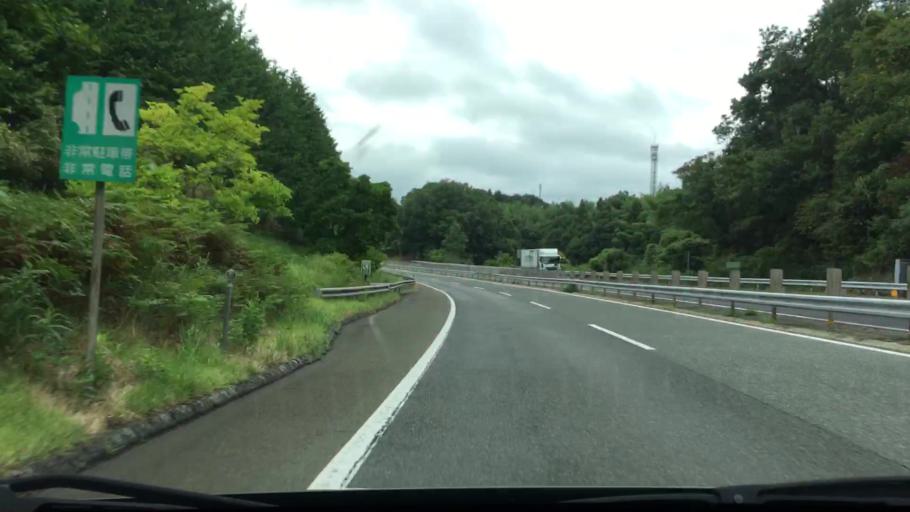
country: JP
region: Hiroshima
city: Shobara
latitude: 34.8418
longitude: 132.9973
